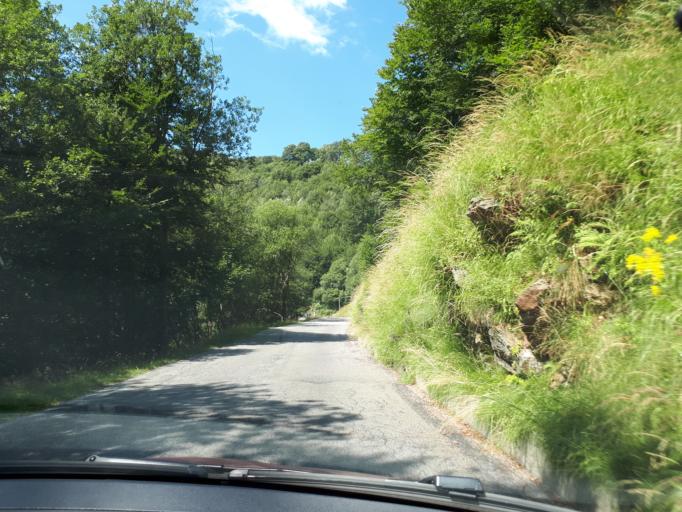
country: CH
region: Ticino
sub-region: Locarno District
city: Magadino
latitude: 46.1066
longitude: 8.8429
